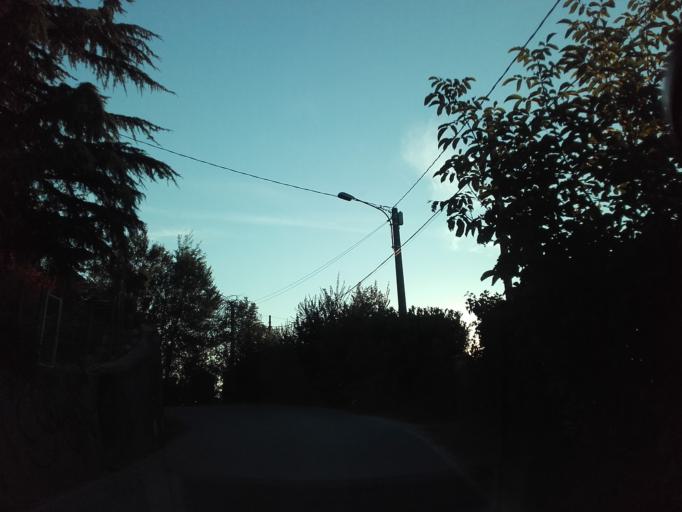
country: IT
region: Piedmont
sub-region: Provincia di Asti
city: Mongardino
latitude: 44.8635
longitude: 8.2135
